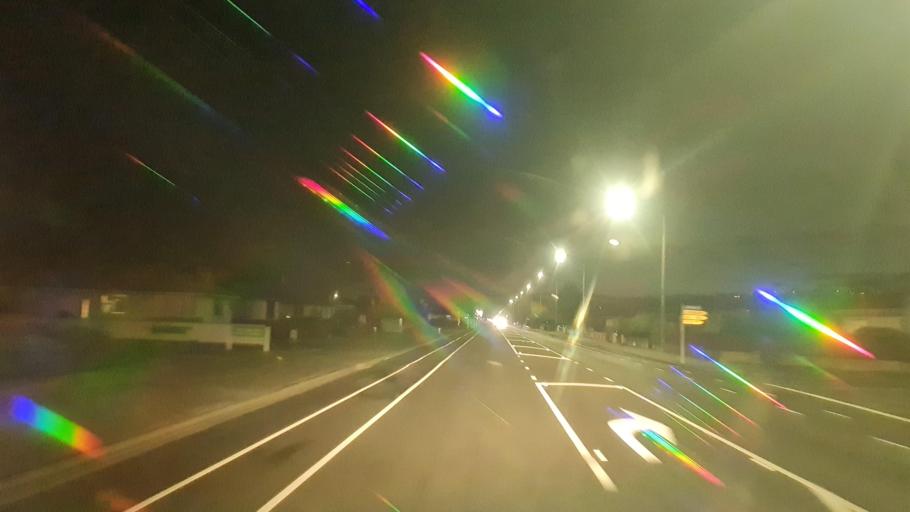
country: NZ
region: Otago
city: Oamaru
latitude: -45.0729
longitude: 170.9894
